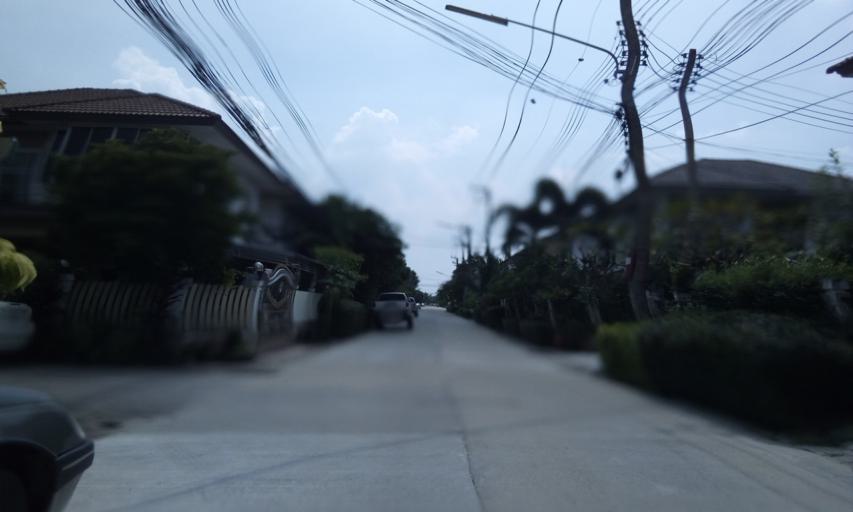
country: TH
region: Pathum Thani
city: Ban Rangsit
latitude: 14.0464
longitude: 100.7653
